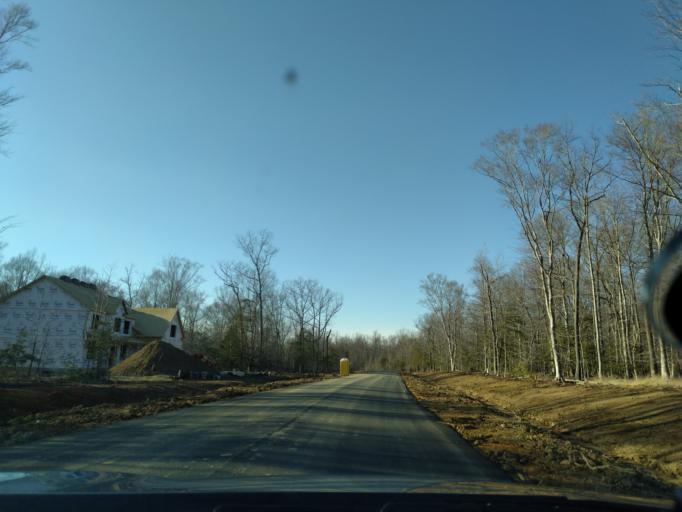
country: US
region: Maryland
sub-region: Charles County
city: La Plata
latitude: 38.4934
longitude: -76.8929
